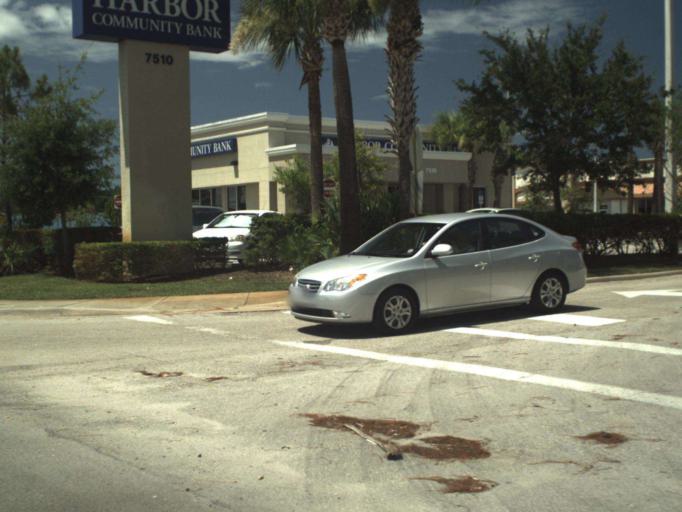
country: US
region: Florida
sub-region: Saint Lucie County
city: River Park
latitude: 27.3286
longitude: -80.3218
